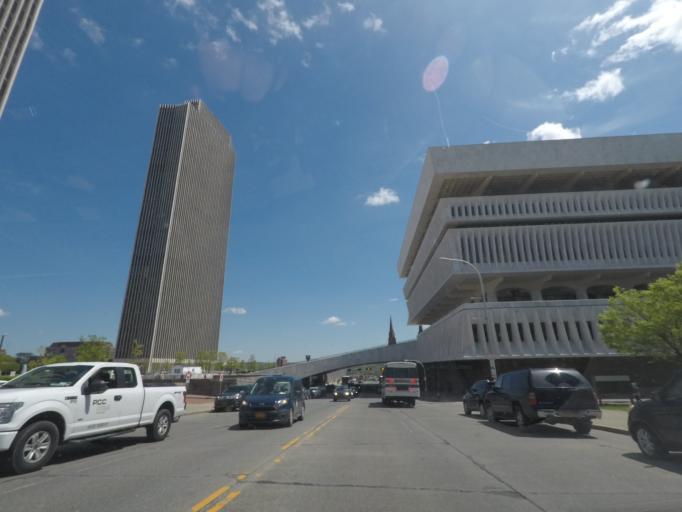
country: US
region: New York
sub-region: Albany County
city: Albany
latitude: 42.6494
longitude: -73.7623
